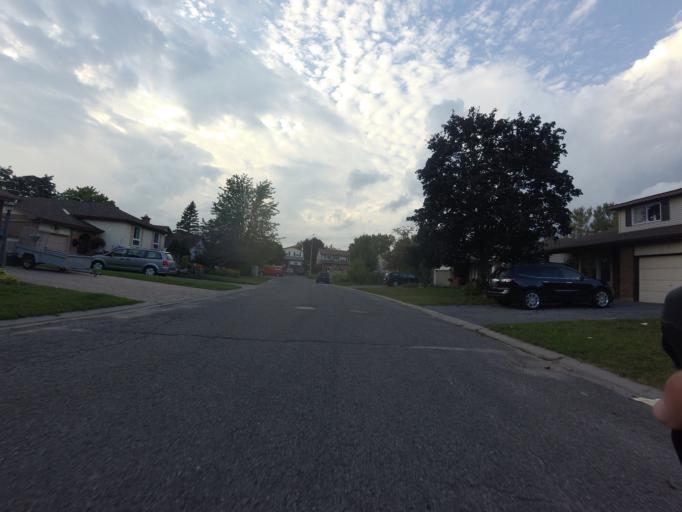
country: CA
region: Ontario
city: Bells Corners
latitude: 45.2767
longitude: -75.7522
